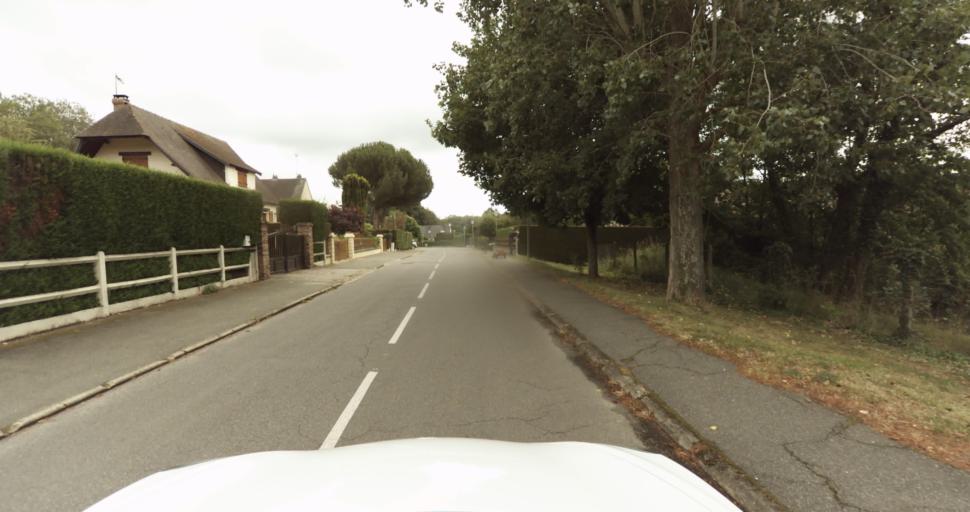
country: FR
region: Haute-Normandie
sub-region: Departement de l'Eure
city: Saint-Sebastien-de-Morsent
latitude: 49.0027
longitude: 1.0917
